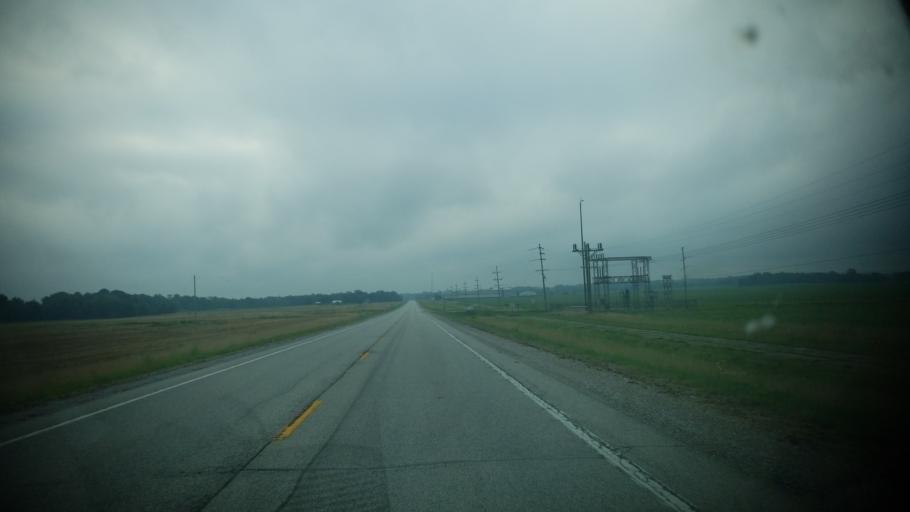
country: US
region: Illinois
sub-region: Clay County
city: Flora
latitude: 38.6776
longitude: -88.3837
